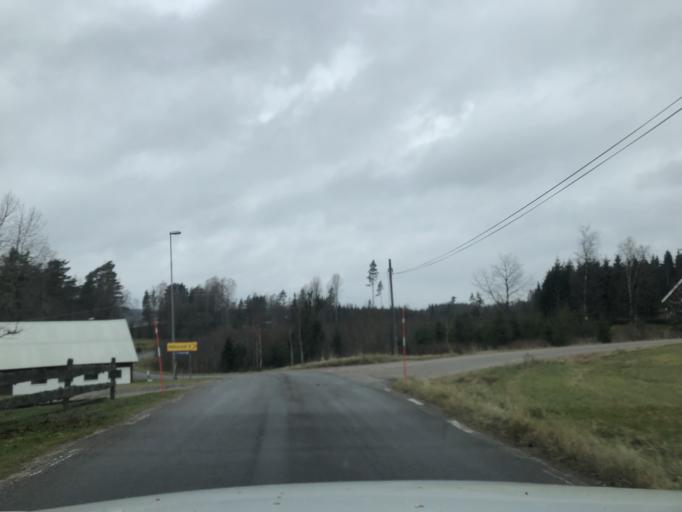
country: SE
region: Vaestra Goetaland
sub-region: Ulricehamns Kommun
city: Ulricehamn
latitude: 57.8647
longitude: 13.5540
